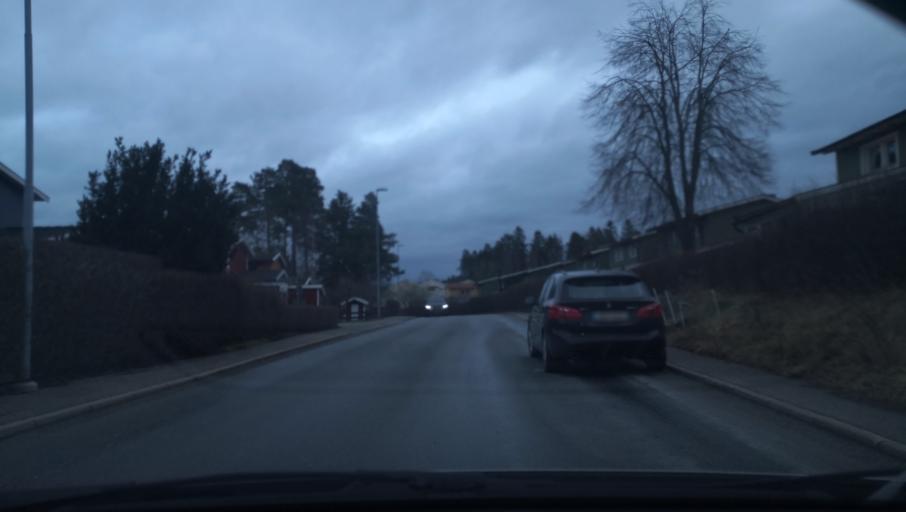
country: SE
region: Stockholm
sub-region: Taby Kommun
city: Taby
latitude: 59.4654
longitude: 18.0375
